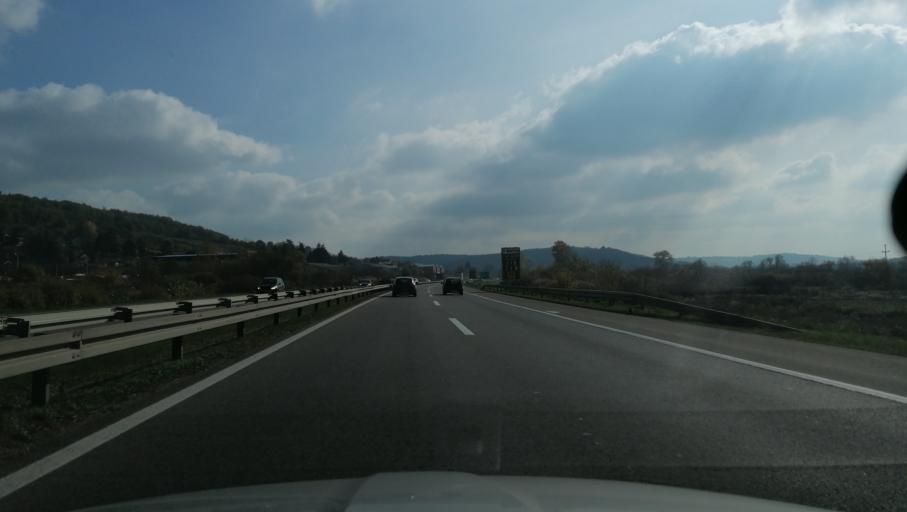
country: RS
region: Central Serbia
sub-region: Belgrade
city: Zvezdara
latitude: 44.7020
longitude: 20.5771
